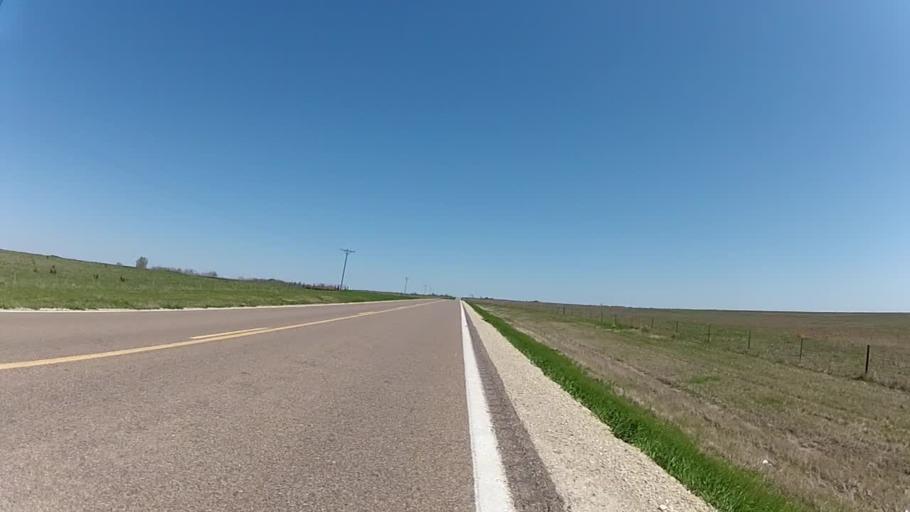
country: US
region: Kansas
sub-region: Wabaunsee County
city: Alma
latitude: 38.9395
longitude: -96.5202
